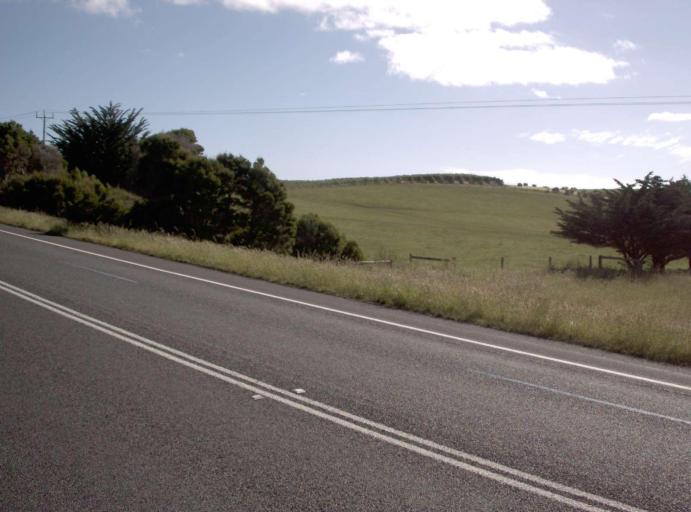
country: AU
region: Victoria
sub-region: Bass Coast
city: North Wonthaggi
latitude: -38.5199
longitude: 145.4480
